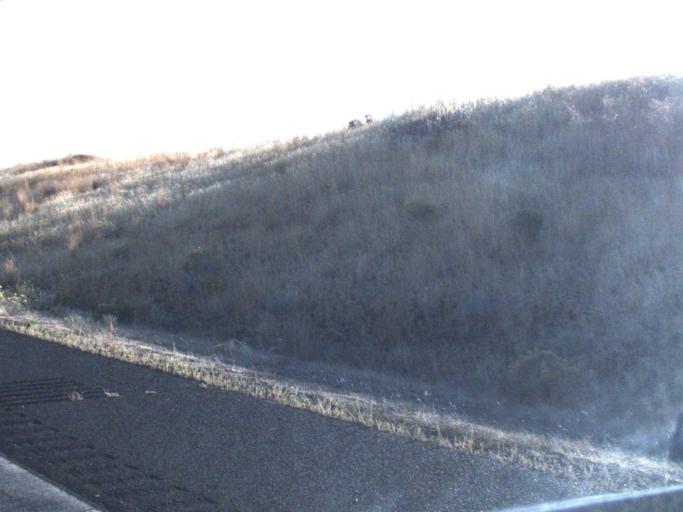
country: US
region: Washington
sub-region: Franklin County
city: Connell
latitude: 46.6067
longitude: -118.9194
